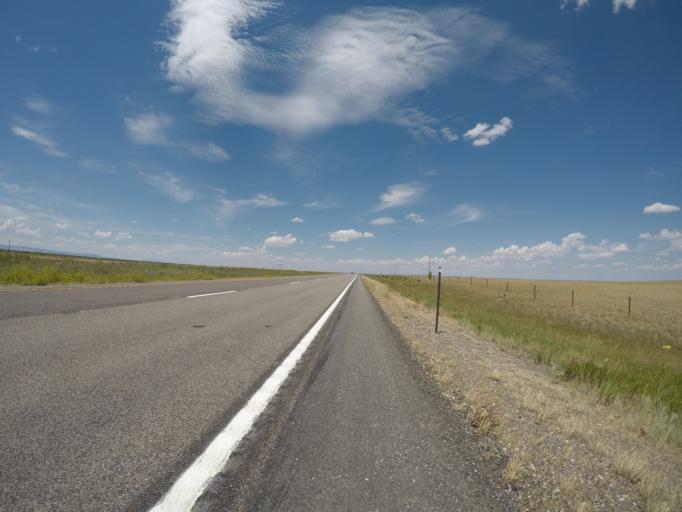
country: US
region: Wyoming
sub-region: Albany County
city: Laramie
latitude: 41.6121
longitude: -105.7363
